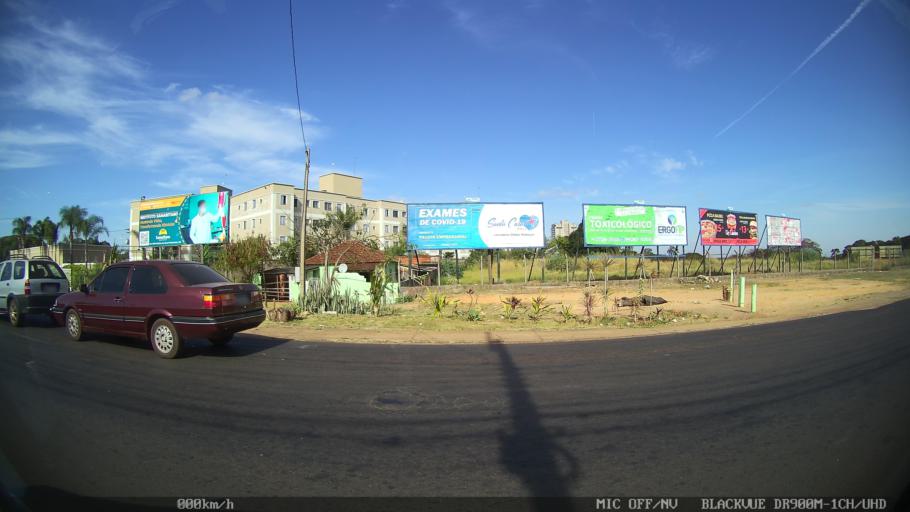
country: BR
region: Sao Paulo
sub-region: Franca
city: Franca
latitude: -20.5423
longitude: -47.4207
